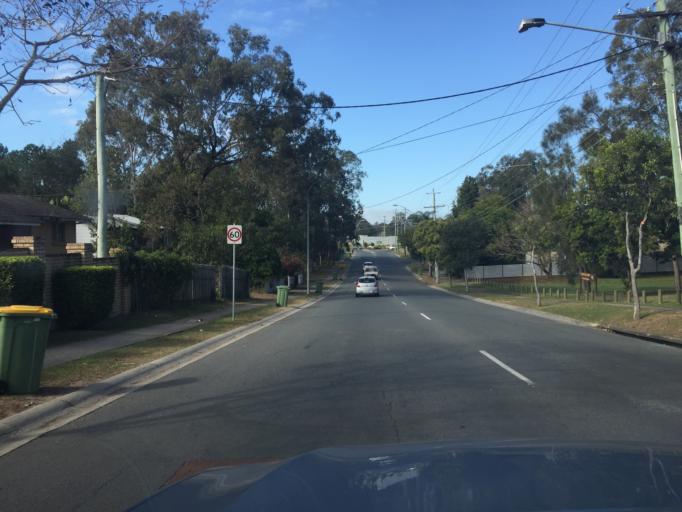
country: AU
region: Queensland
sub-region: Logan
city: Slacks Creek
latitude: -27.6452
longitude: 153.1532
